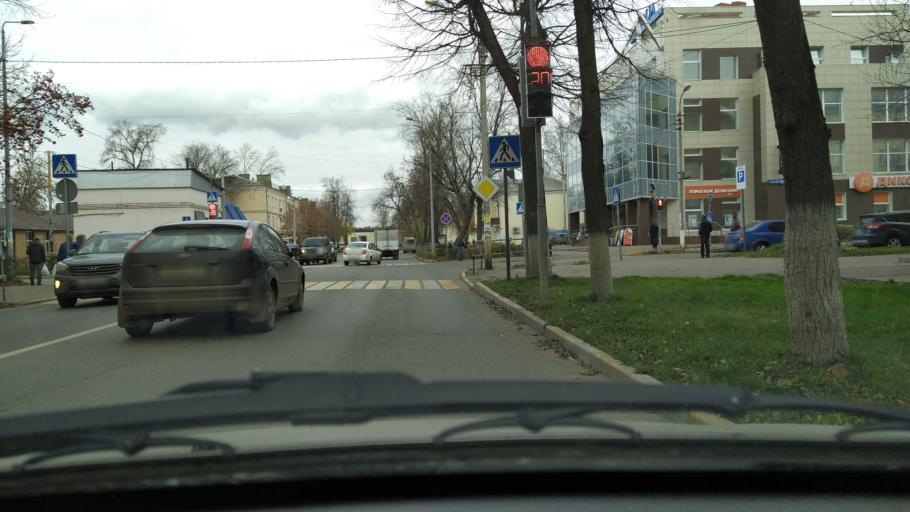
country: RU
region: Moskovskaya
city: Voskresensk
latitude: 55.3236
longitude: 38.6816
